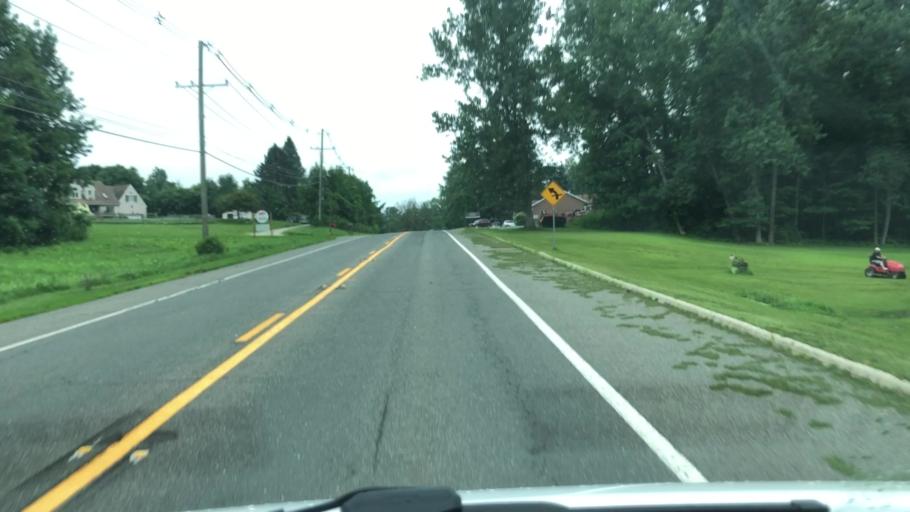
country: US
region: Massachusetts
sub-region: Berkshire County
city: Lanesborough
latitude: 42.5422
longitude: -73.2316
